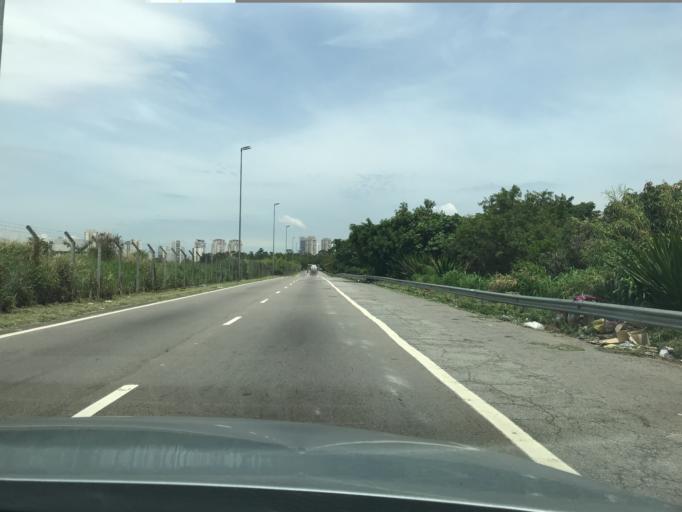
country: BR
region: Sao Paulo
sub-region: Osasco
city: Osasco
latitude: -23.5109
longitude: -46.7379
